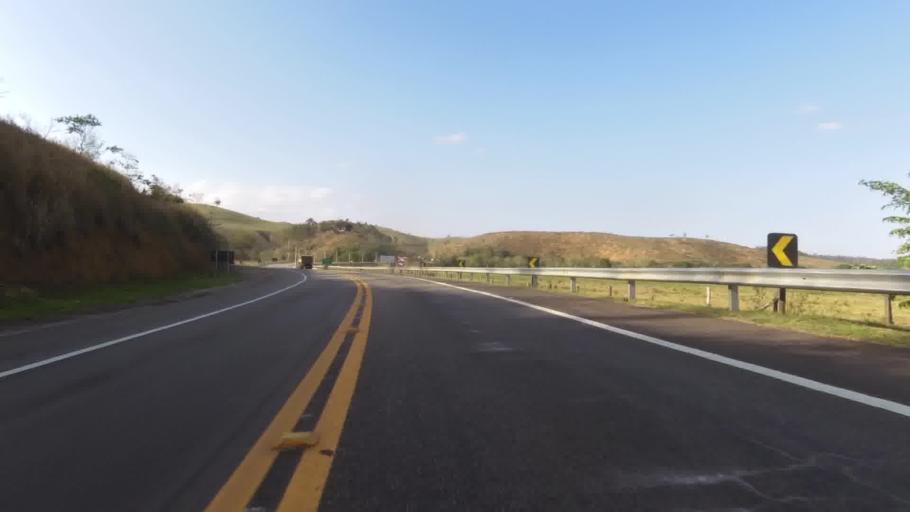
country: BR
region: Espirito Santo
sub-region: Mimoso Do Sul
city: Mimoso do Sul
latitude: -21.2266
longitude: -41.3119
